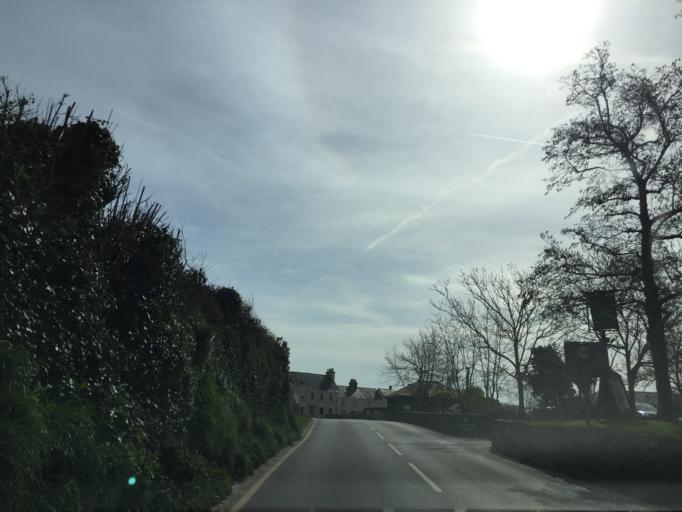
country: JE
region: St Helier
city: Saint Helier
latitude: 49.2332
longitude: -2.0905
